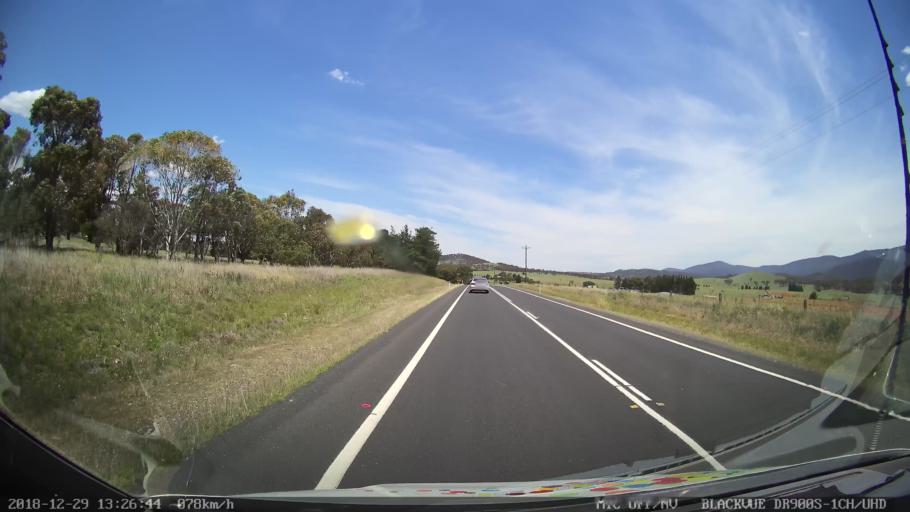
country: AU
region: New South Wales
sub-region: Cooma-Monaro
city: Cooma
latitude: -35.8589
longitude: 149.1581
